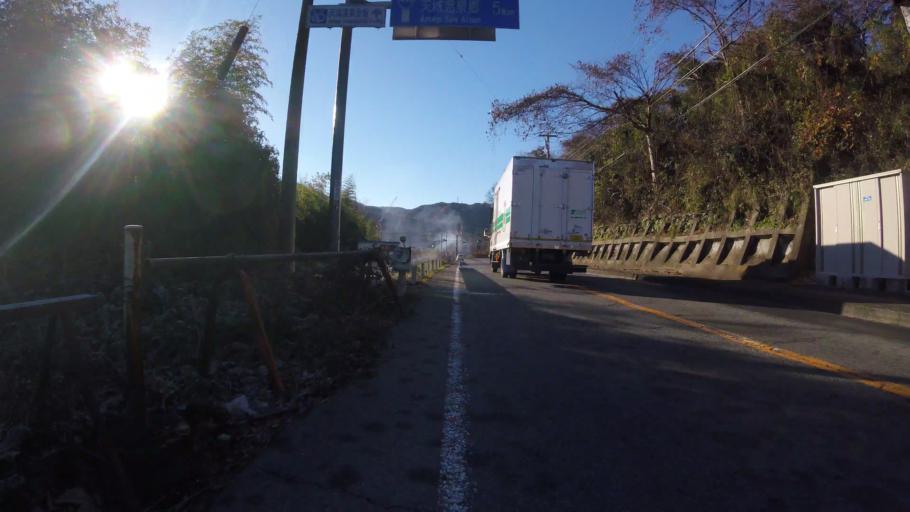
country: JP
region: Shizuoka
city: Heda
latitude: 34.9264
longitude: 138.9324
